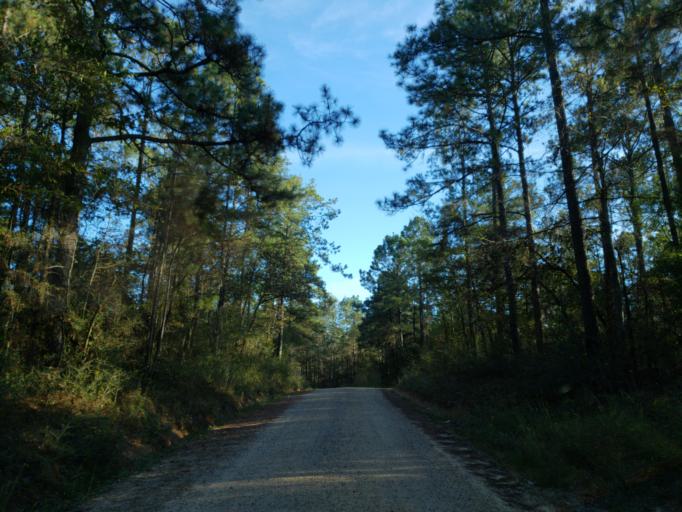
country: US
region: Mississippi
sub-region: Perry County
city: Richton
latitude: 31.3423
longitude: -88.7983
